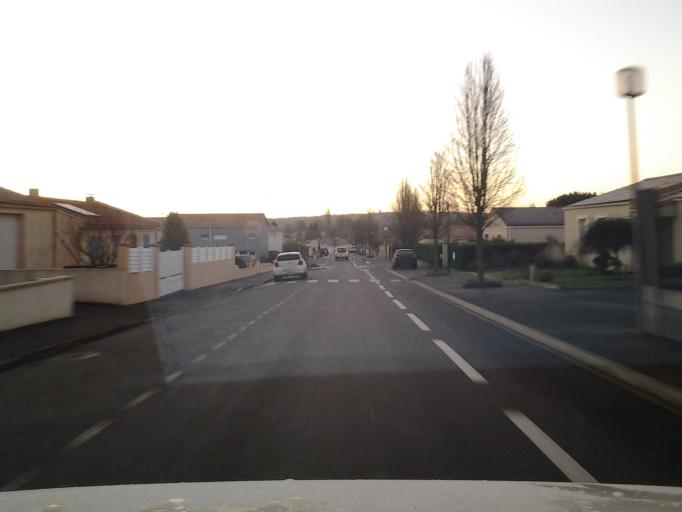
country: FR
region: Pays de la Loire
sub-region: Departement de la Vendee
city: Les Epesses
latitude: 46.8810
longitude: -0.9053
